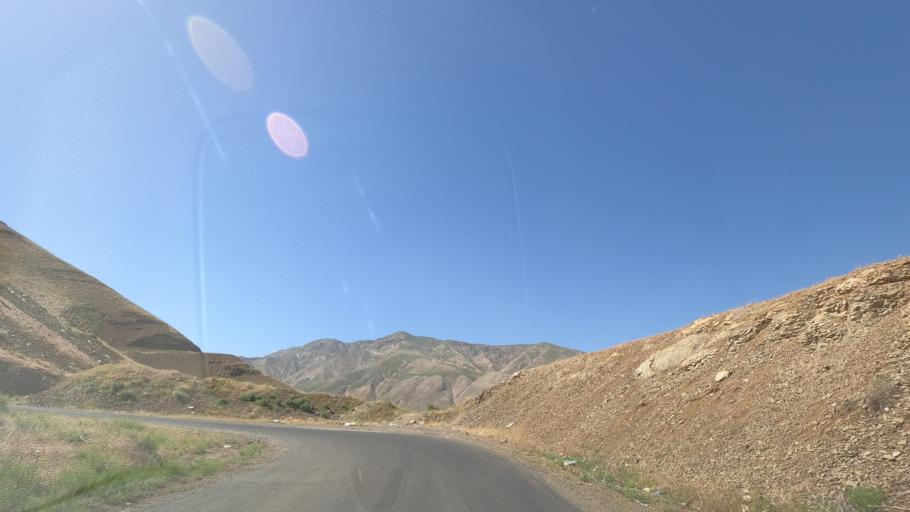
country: IR
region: Alborz
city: Karaj
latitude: 35.9384
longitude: 51.0791
